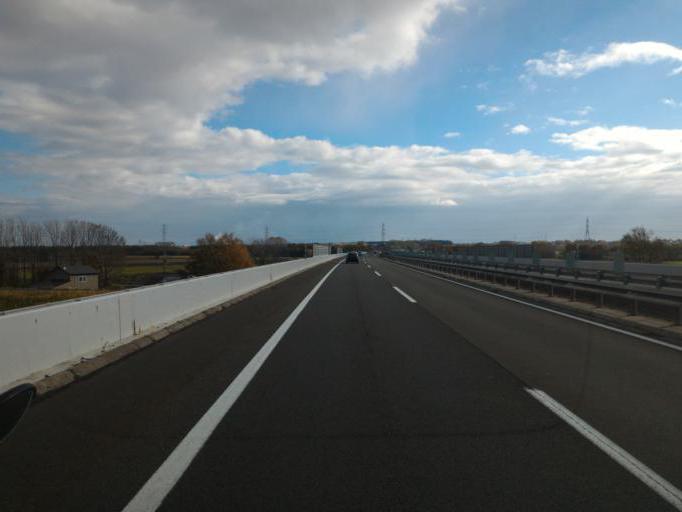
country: JP
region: Hokkaido
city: Ebetsu
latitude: 43.0940
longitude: 141.4753
